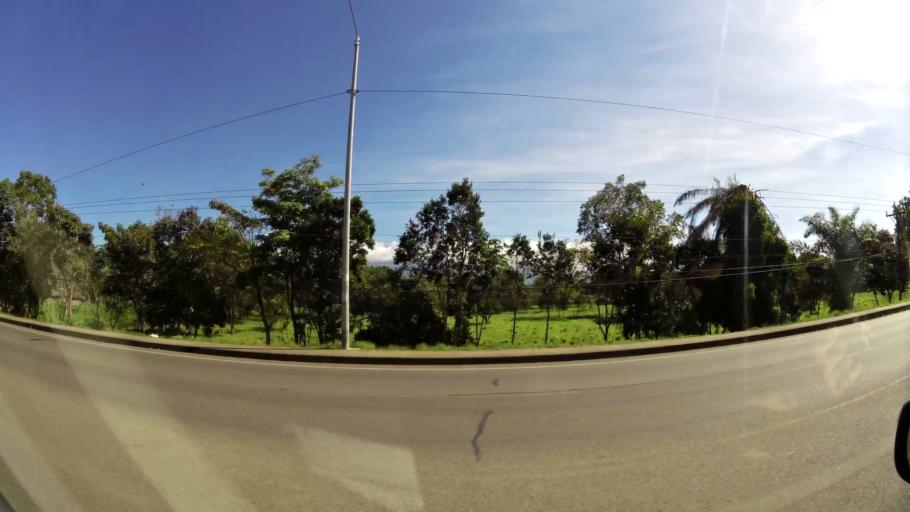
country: CR
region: San Jose
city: Daniel Flores
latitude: 9.3310
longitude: -83.6692
